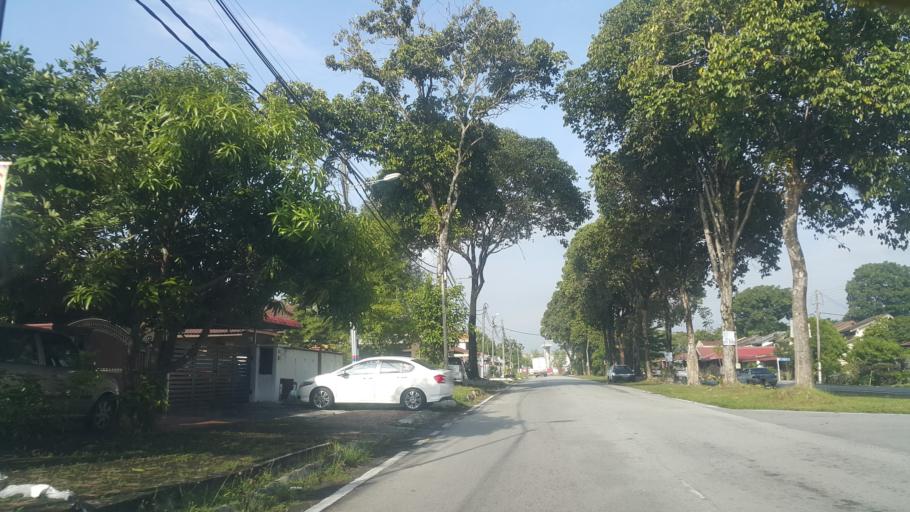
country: MY
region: Selangor
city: Klang
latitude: 3.0123
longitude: 101.4421
